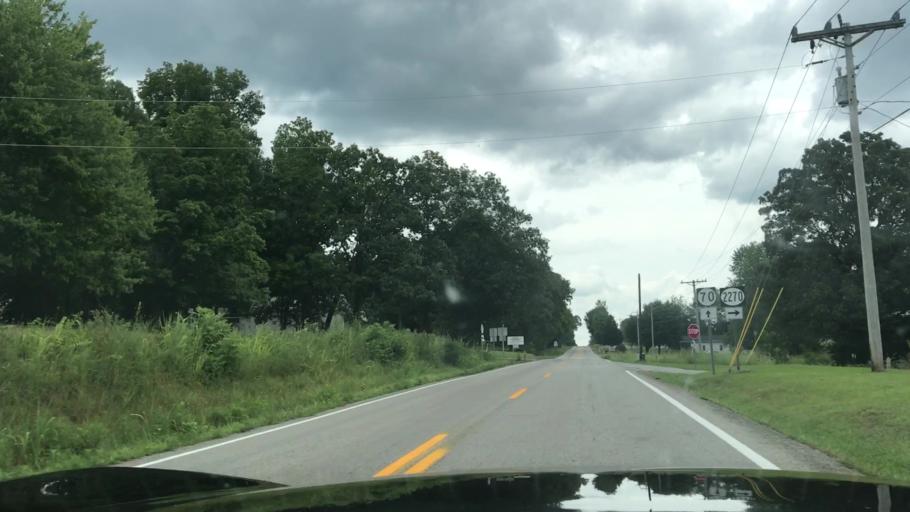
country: US
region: Kentucky
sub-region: Muhlenberg County
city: Central City
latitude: 37.1991
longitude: -86.9732
